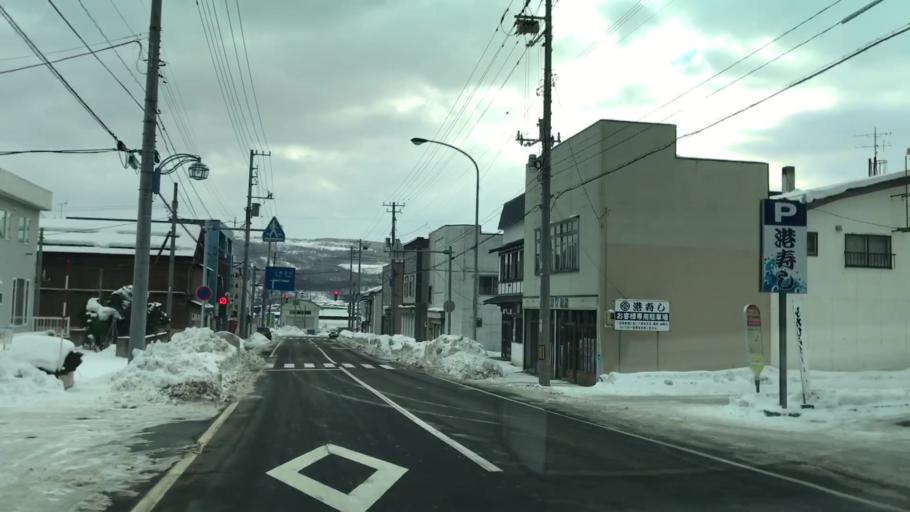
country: JP
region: Hokkaido
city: Yoichi
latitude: 43.2783
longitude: 140.6379
